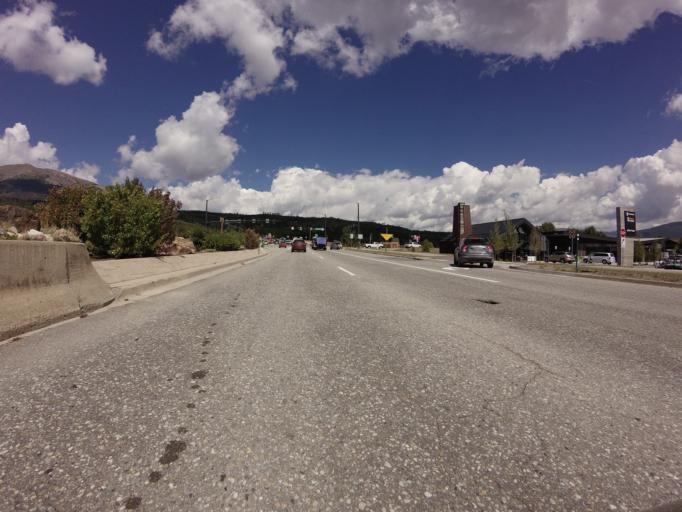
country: US
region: Colorado
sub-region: Summit County
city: Frisco
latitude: 39.5902
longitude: -106.0953
